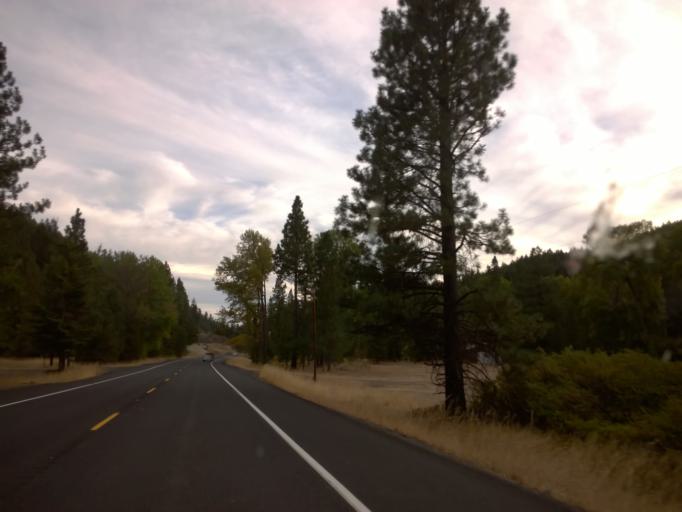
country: US
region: Washington
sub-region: Kittitas County
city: Cle Elum
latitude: 47.2336
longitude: -120.6951
